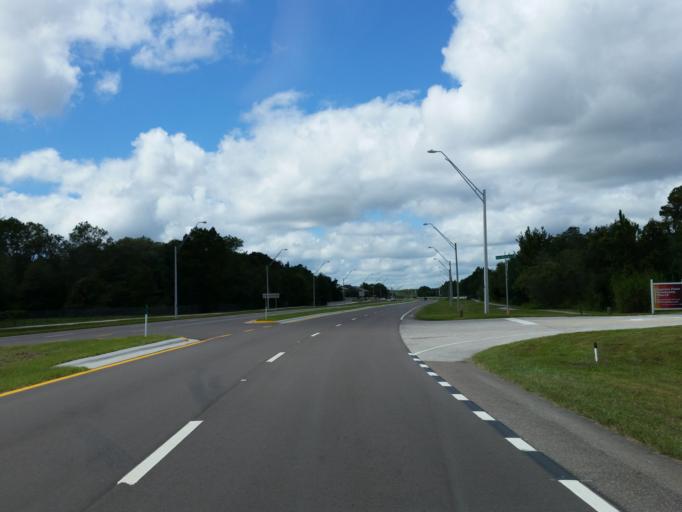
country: US
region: Florida
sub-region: Hillsborough County
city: Pebble Creek
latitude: 28.1441
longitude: -82.2838
